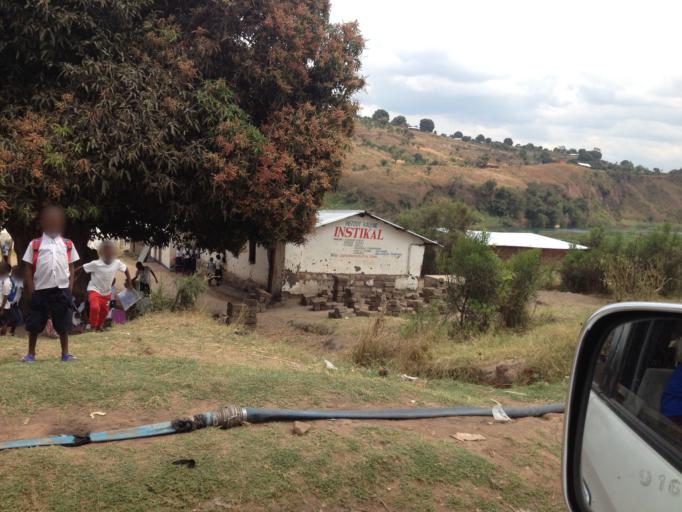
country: CD
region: Katanga
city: Kalemie
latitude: -5.9177
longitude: 29.1792
